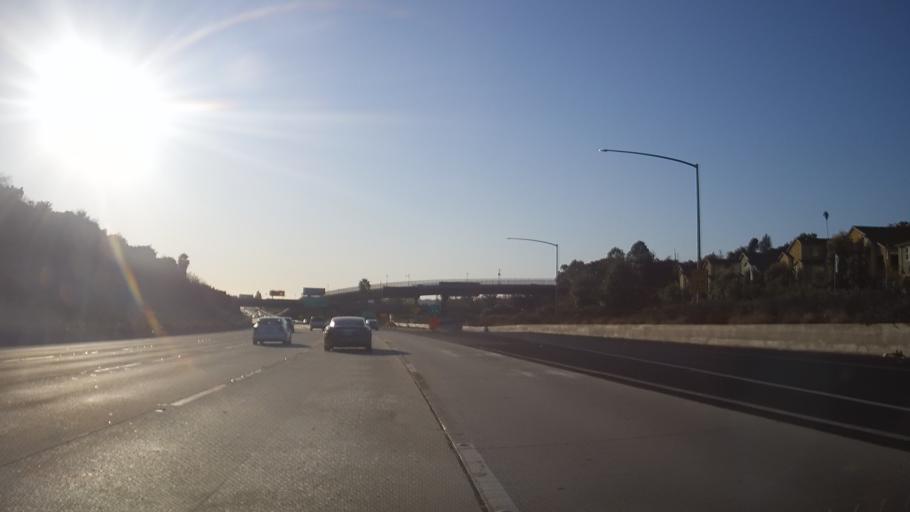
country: US
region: California
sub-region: San Diego County
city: La Mesa
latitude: 32.7818
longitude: -117.0841
